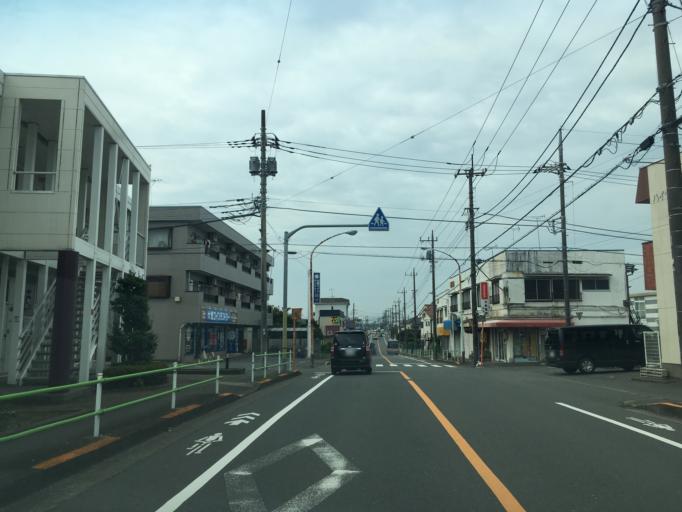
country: JP
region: Tokyo
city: Higashimurayama-shi
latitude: 35.7533
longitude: 139.3991
